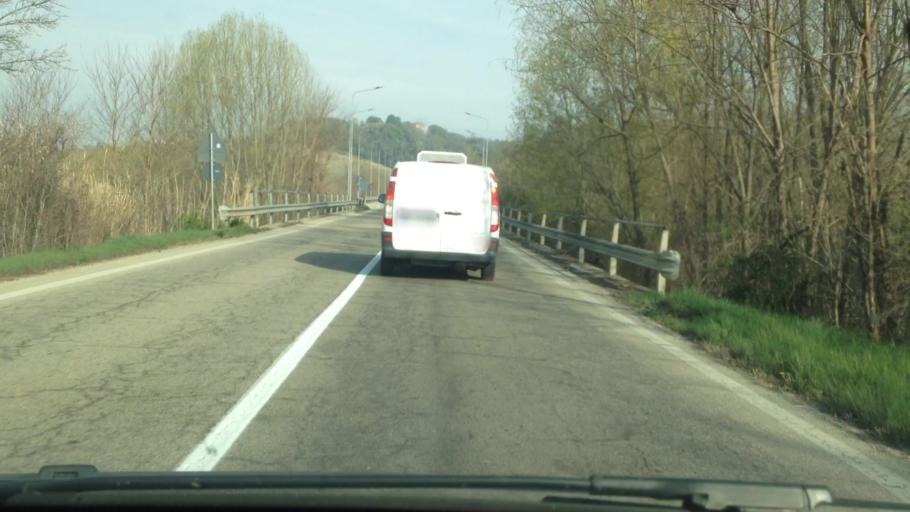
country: IT
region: Piedmont
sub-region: Provincia di Cuneo
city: Canale
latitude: 44.8012
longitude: 7.9792
